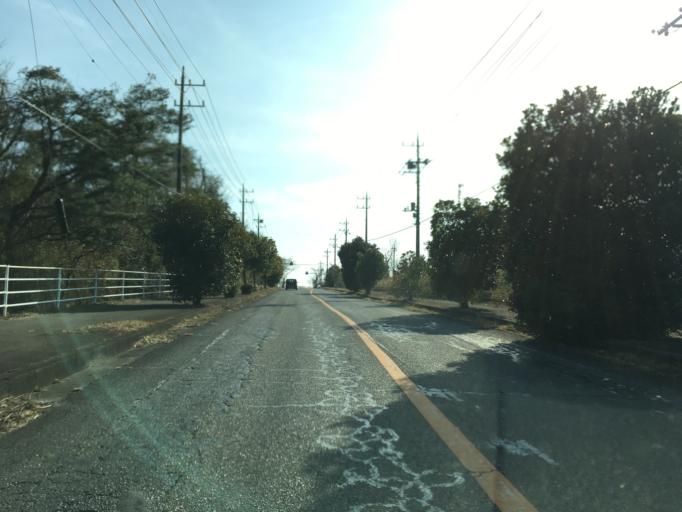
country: JP
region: Ibaraki
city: Takahagi
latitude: 36.7534
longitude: 140.7068
